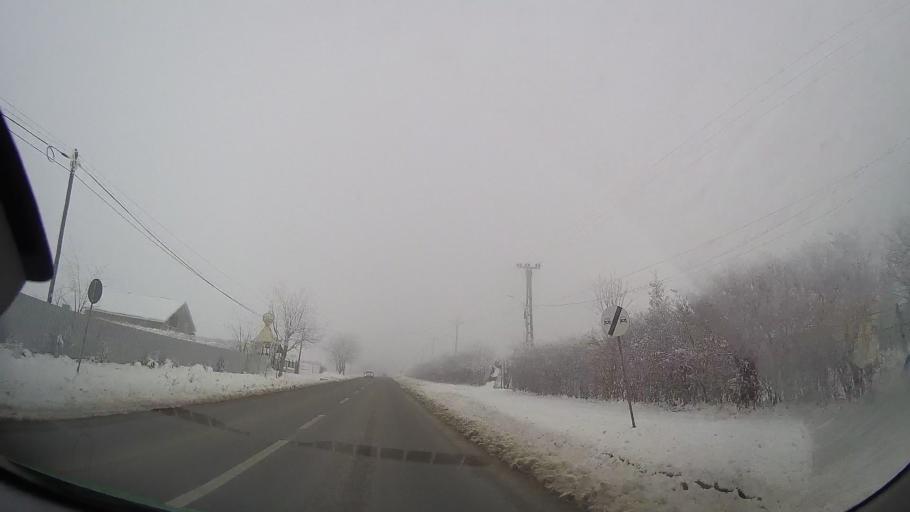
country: RO
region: Iasi
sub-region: Comuna Stolniceni-Prajescu
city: Stolniceni-Prajescu
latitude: 47.1968
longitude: 26.7387
